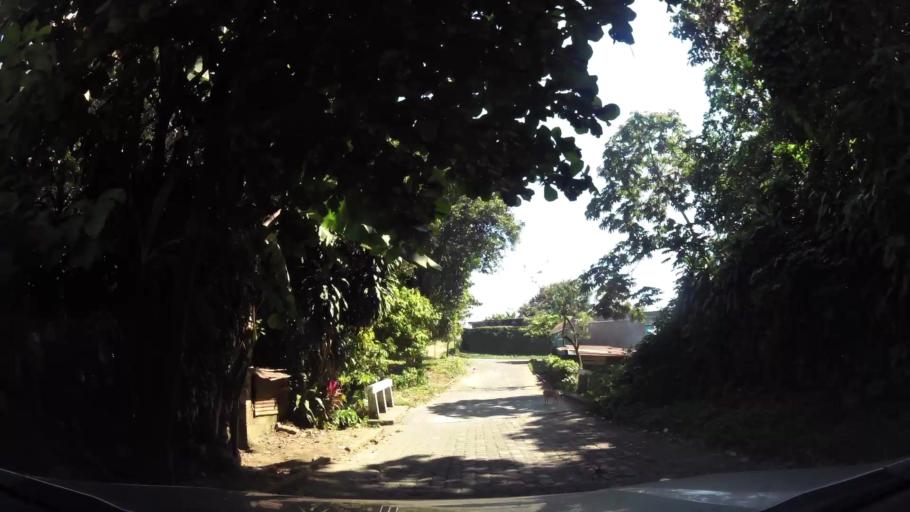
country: GT
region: Suchitepeque
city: Mazatenango
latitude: 14.5314
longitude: -91.4946
